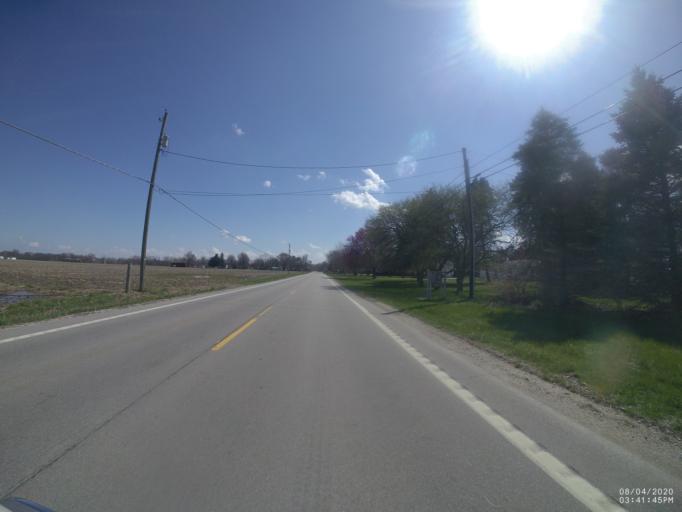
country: US
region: Ohio
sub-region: Sandusky County
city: Stony Prairie
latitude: 41.2567
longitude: -83.2357
